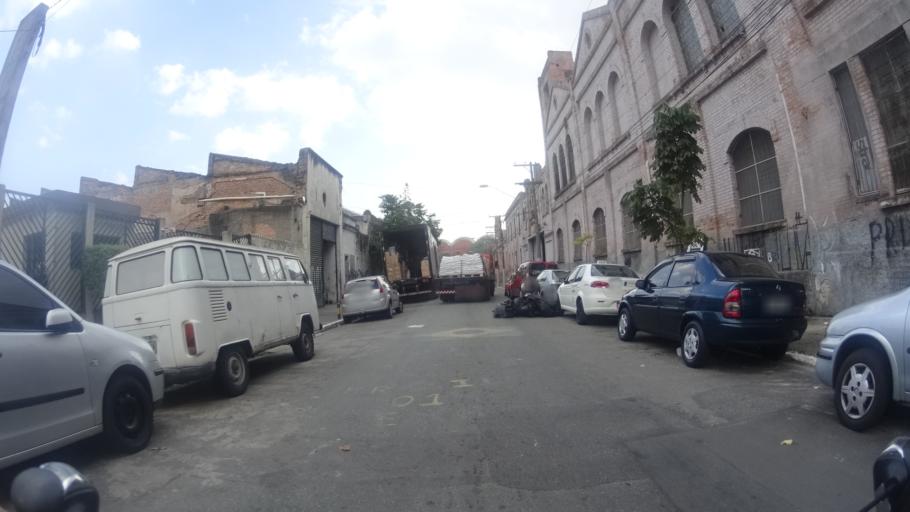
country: BR
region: Sao Paulo
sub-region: Sao Paulo
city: Sao Paulo
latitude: -23.5407
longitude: -46.6210
